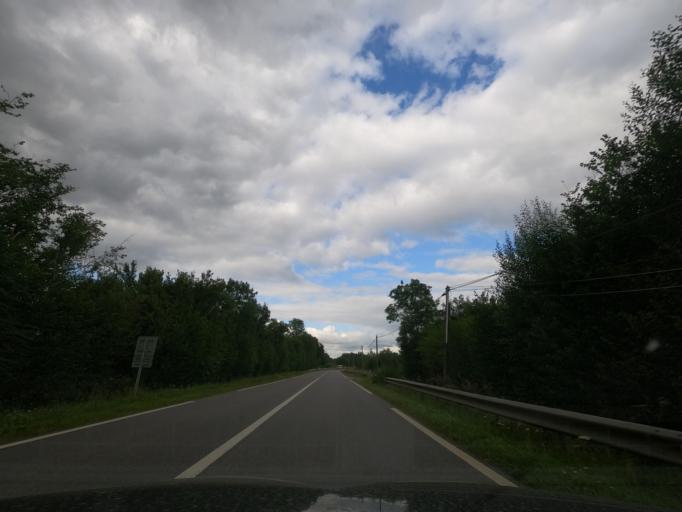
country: FR
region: Lower Normandy
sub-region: Departement de l'Orne
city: Gace
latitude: 48.8693
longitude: 0.3761
